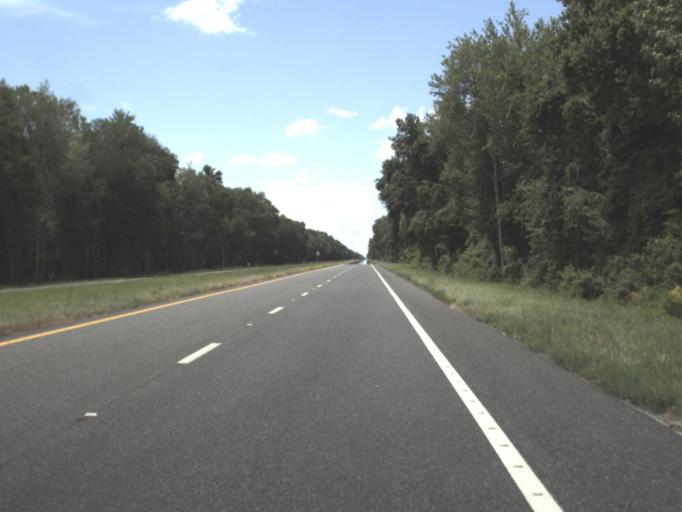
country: US
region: Florida
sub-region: Taylor County
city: Perry
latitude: 30.2374
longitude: -83.6883
